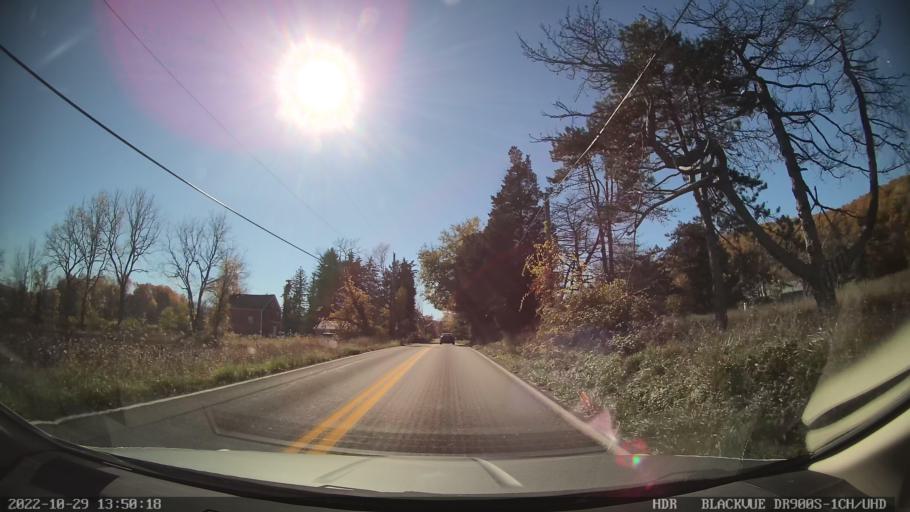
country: US
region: Pennsylvania
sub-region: Lehigh County
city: Emmaus
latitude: 40.5359
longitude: -75.4587
